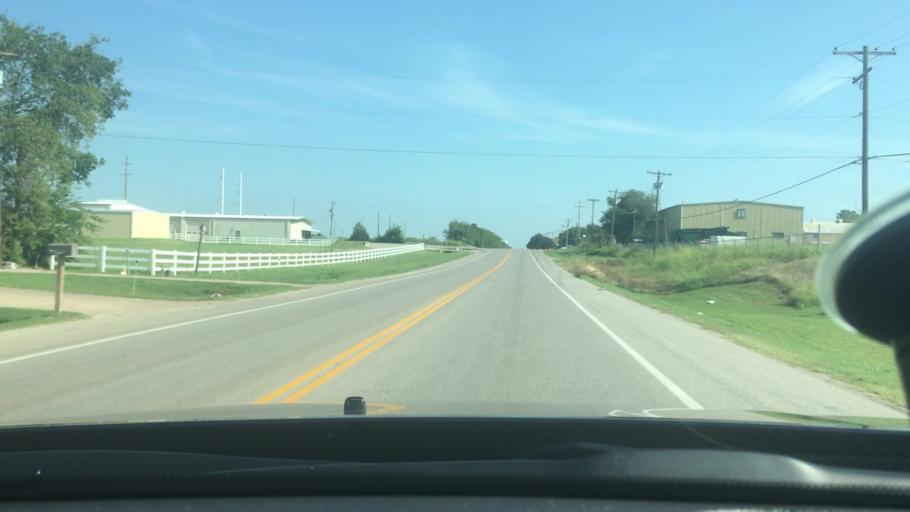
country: US
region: Oklahoma
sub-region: Garvin County
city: Pauls Valley
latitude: 34.7077
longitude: -97.2129
